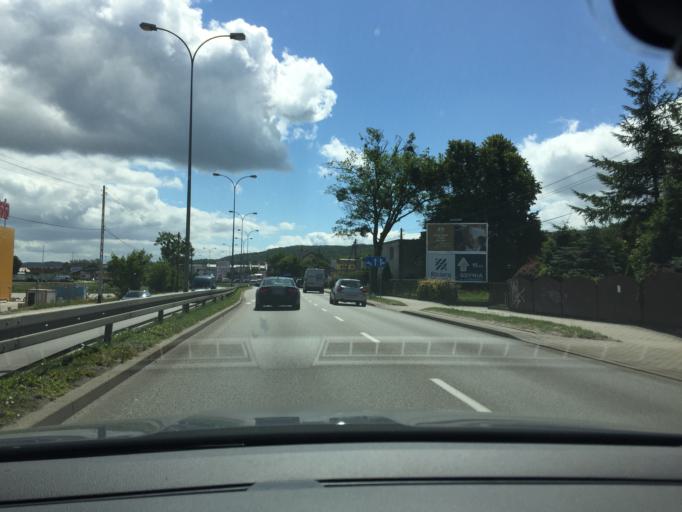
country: PL
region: Pomeranian Voivodeship
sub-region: Powiat wejherowski
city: Reda
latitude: 54.5859
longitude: 18.3626
